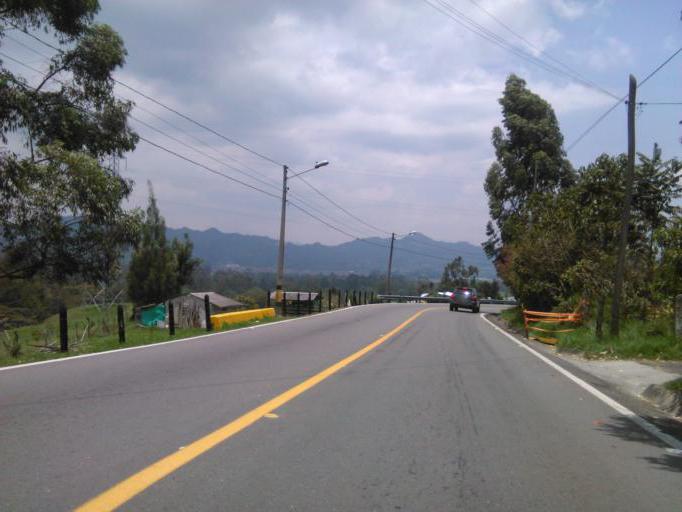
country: CO
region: Antioquia
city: La Ceja
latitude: 6.0155
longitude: -75.4052
